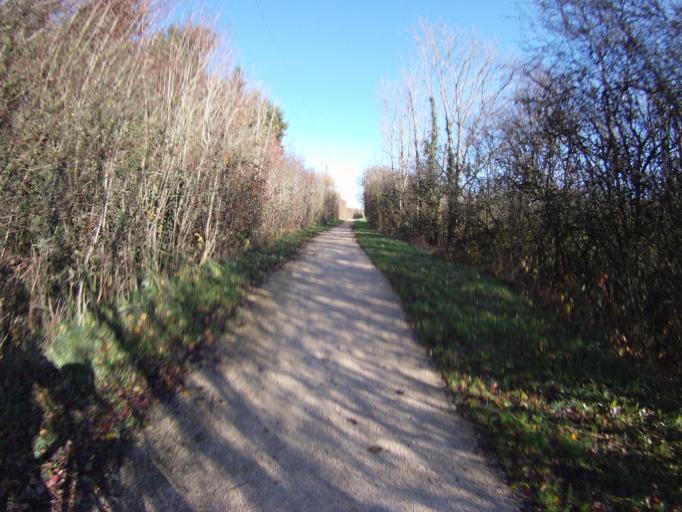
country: FR
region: Lorraine
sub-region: Departement de Meurthe-et-Moselle
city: Bouxieres-aux-Chenes
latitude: 48.7949
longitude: 6.2350
